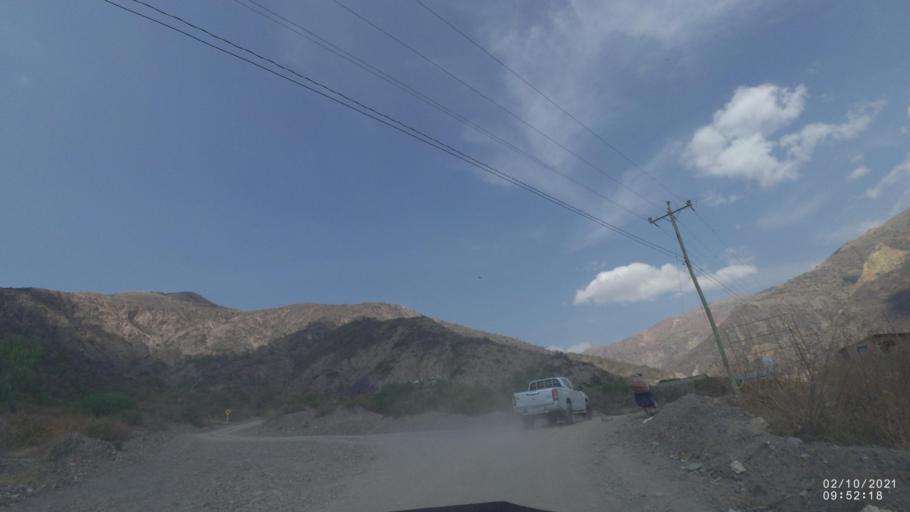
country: BO
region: Cochabamba
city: Irpa Irpa
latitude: -17.8005
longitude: -66.3436
